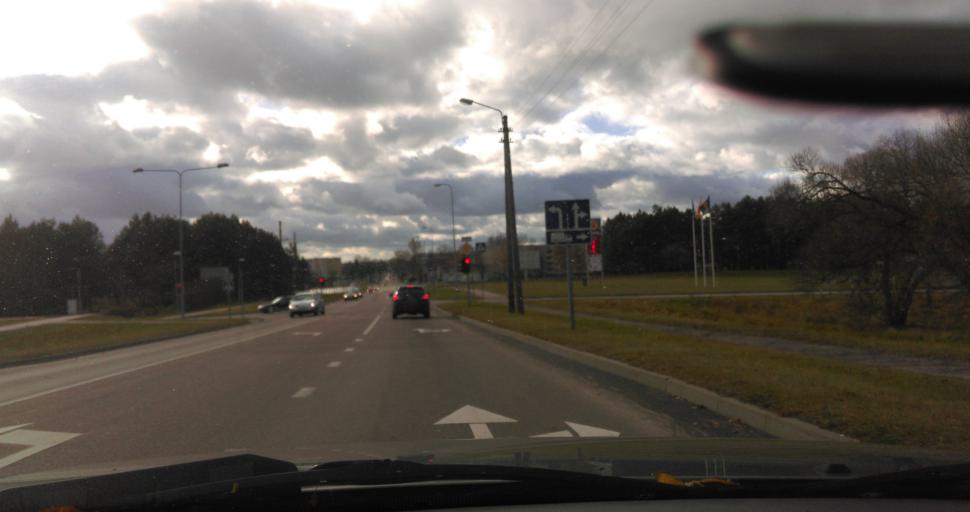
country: LT
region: Utenos apskritis
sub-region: Utena
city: Utena
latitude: 55.5048
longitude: 25.6232
